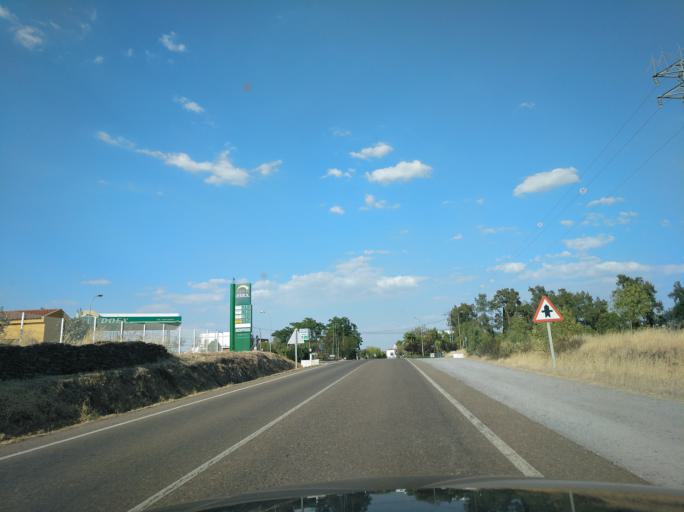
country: ES
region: Extremadura
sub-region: Provincia de Badajoz
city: Villanueva del Fresno
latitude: 38.3785
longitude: -7.1684
